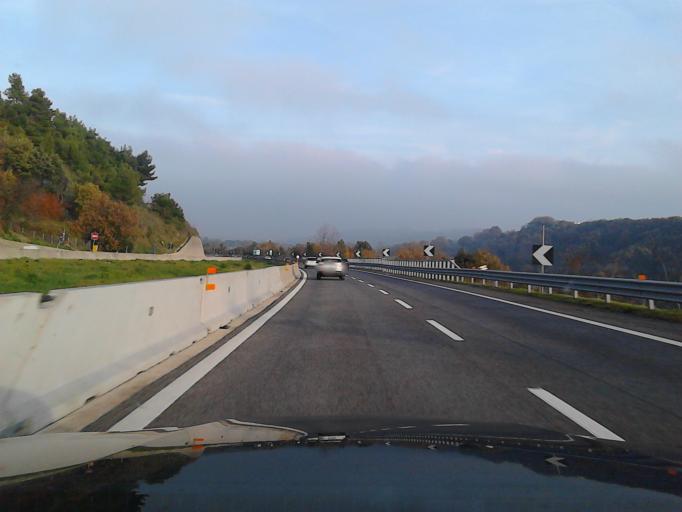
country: IT
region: Abruzzo
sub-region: Provincia di Chieti
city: Torrevecchia
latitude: 42.4144
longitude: 14.2359
